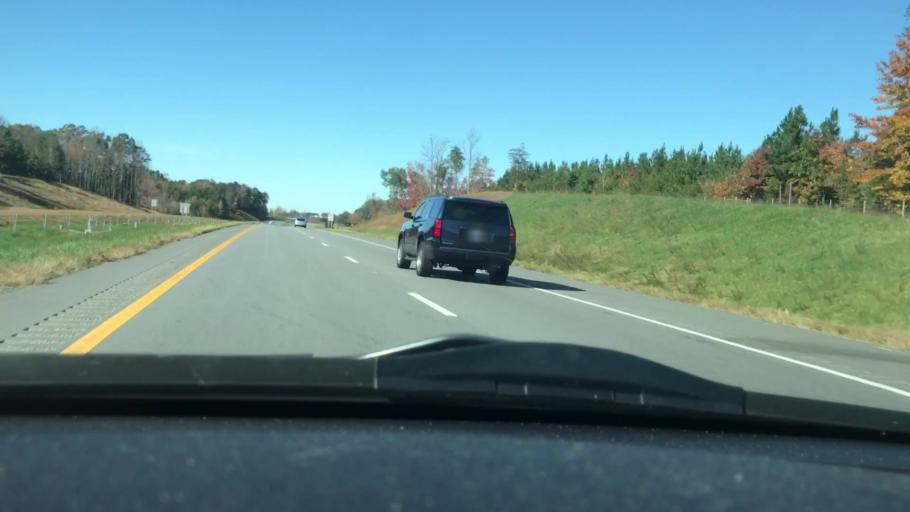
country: US
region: North Carolina
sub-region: Guilford County
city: Stokesdale
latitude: 36.2757
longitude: -79.9350
